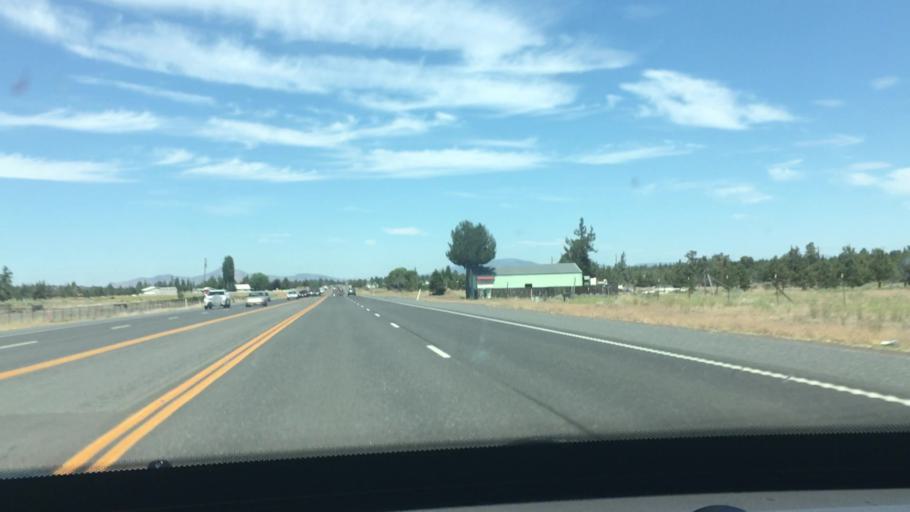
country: US
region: Oregon
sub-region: Deschutes County
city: Redmond
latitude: 44.2106
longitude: -121.2210
